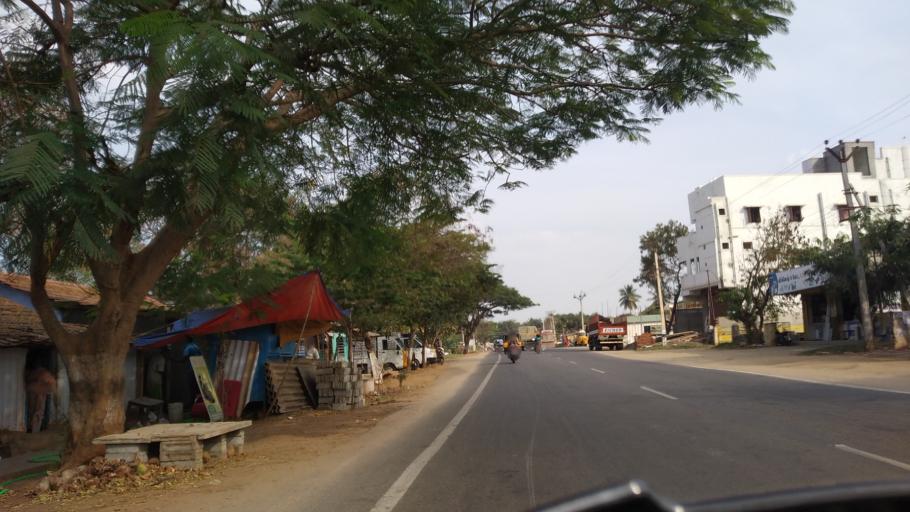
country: IN
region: Tamil Nadu
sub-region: Coimbatore
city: Perur
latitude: 10.9688
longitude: 76.8990
